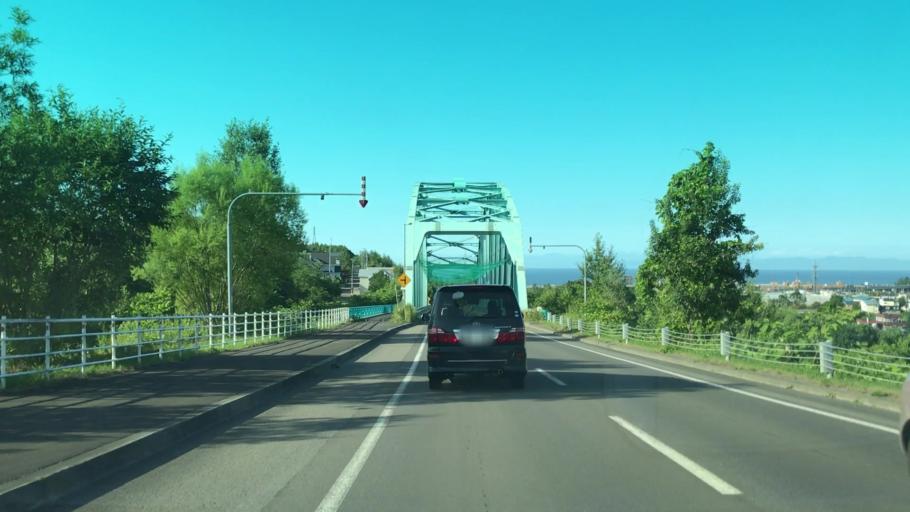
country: JP
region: Hokkaido
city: Otaru
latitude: 43.1605
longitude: 141.0430
